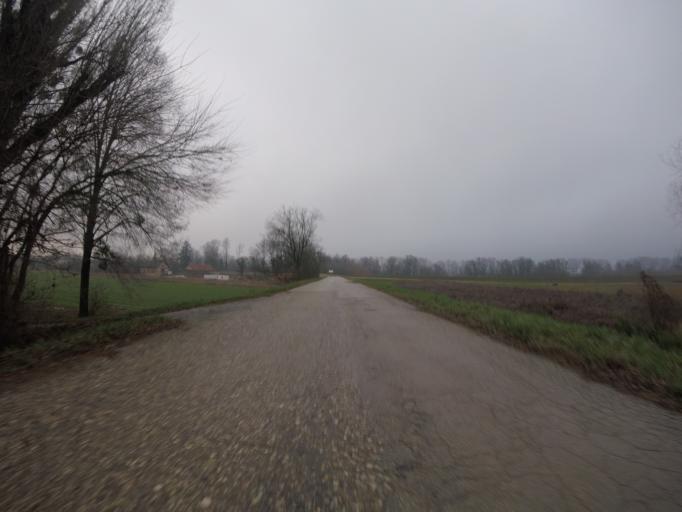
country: HR
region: Zagrebacka
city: Kuce
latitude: 45.7103
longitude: 16.2200
